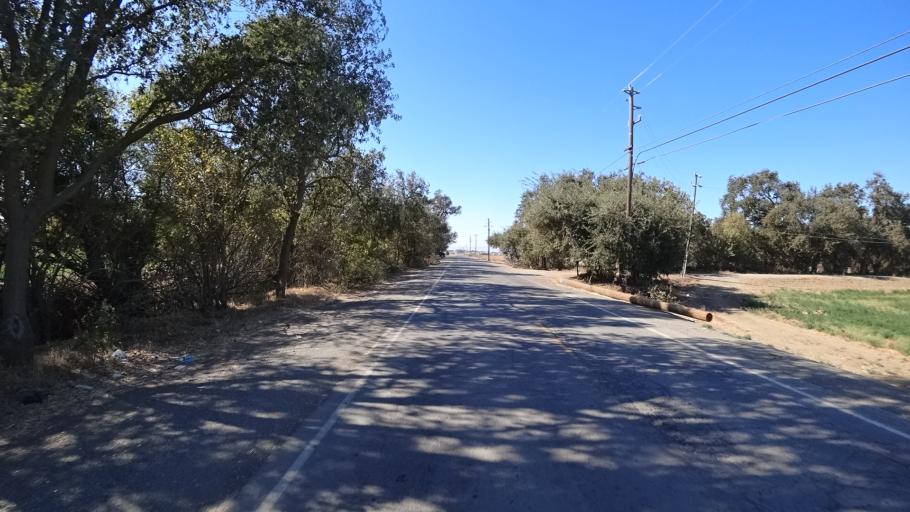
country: US
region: California
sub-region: Yolo County
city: Woodland
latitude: 38.6192
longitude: -121.7426
